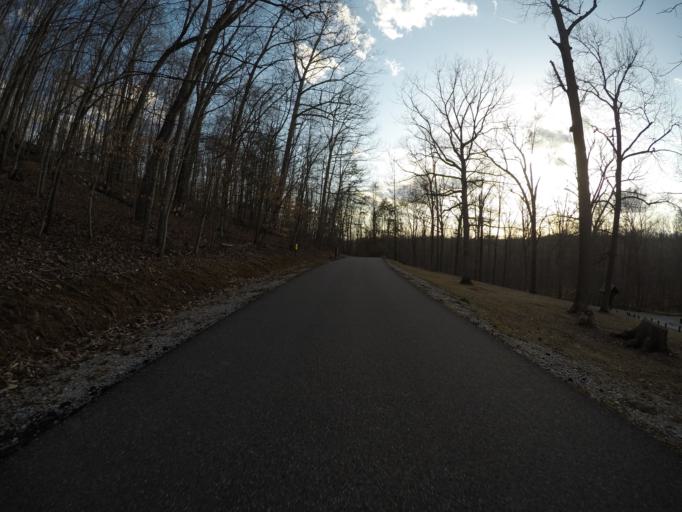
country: US
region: West Virginia
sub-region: Kanawha County
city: Charleston
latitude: 38.3912
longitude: -81.5686
